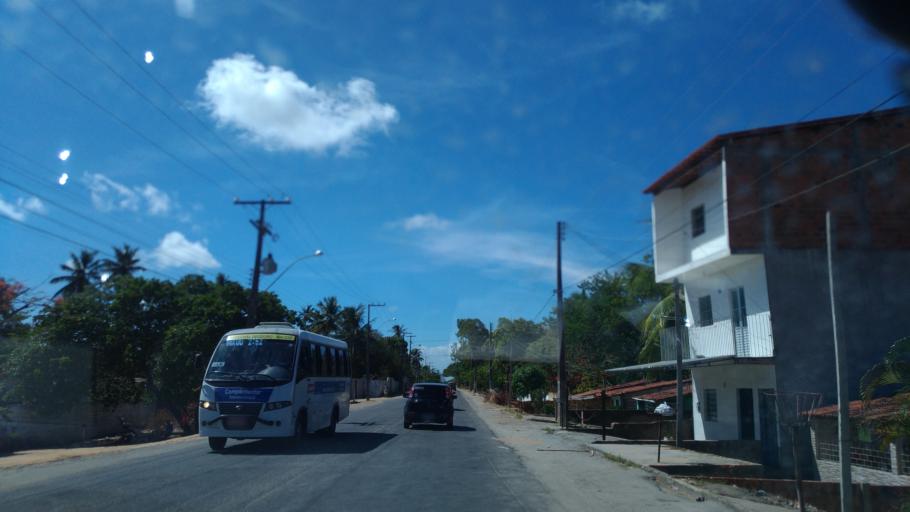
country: BR
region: Alagoas
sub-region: Marechal Deodoro
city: Marechal Deodoro
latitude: -9.7590
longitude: -35.8681
